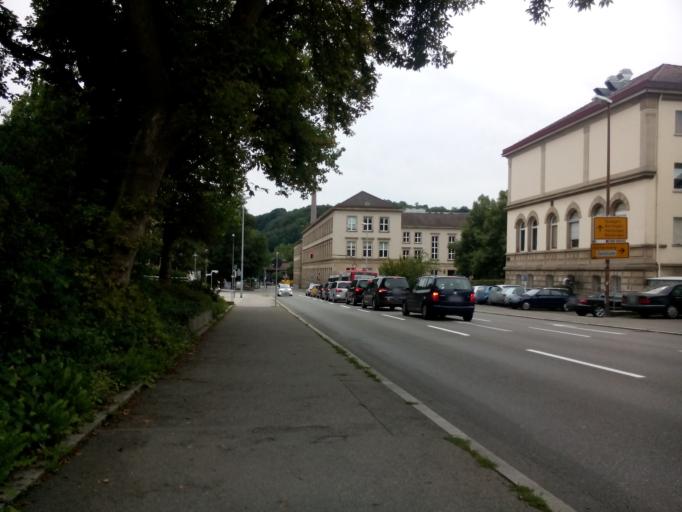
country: DE
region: Baden-Wuerttemberg
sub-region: Tuebingen Region
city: Tuebingen
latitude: 48.5259
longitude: 9.0575
